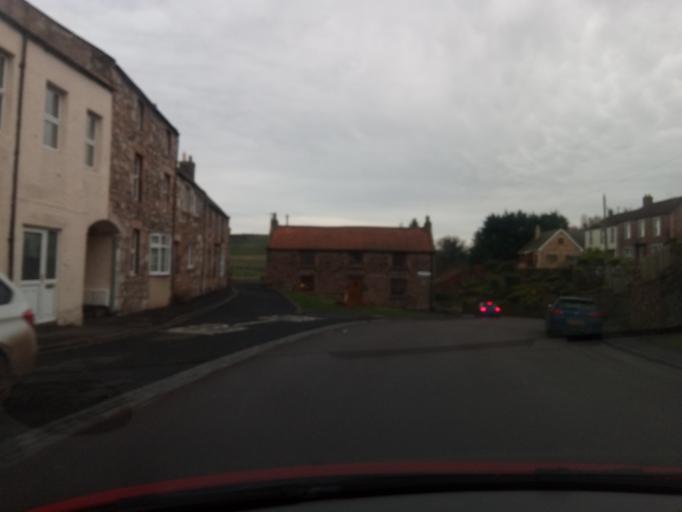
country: GB
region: England
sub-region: Northumberland
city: Wooler
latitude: 55.5453
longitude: -2.0141
